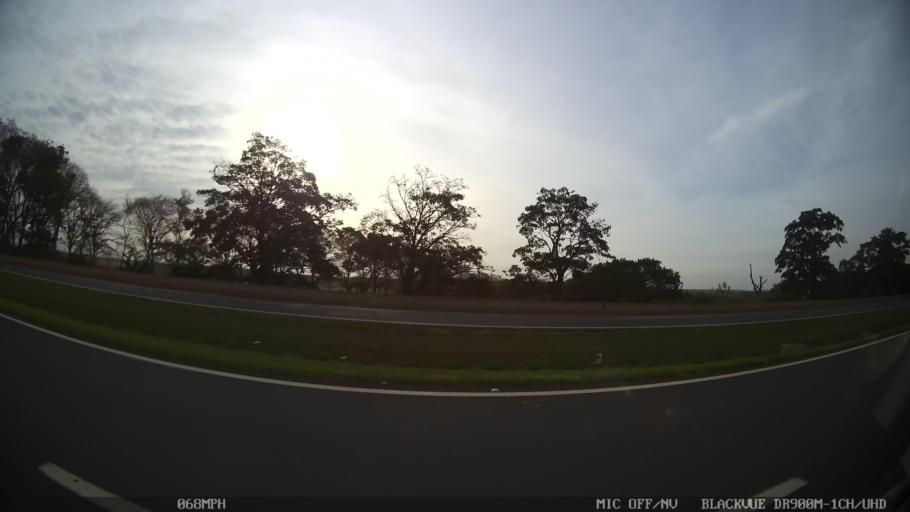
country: BR
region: Sao Paulo
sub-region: Piracicaba
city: Piracicaba
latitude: -22.6753
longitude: -47.5607
